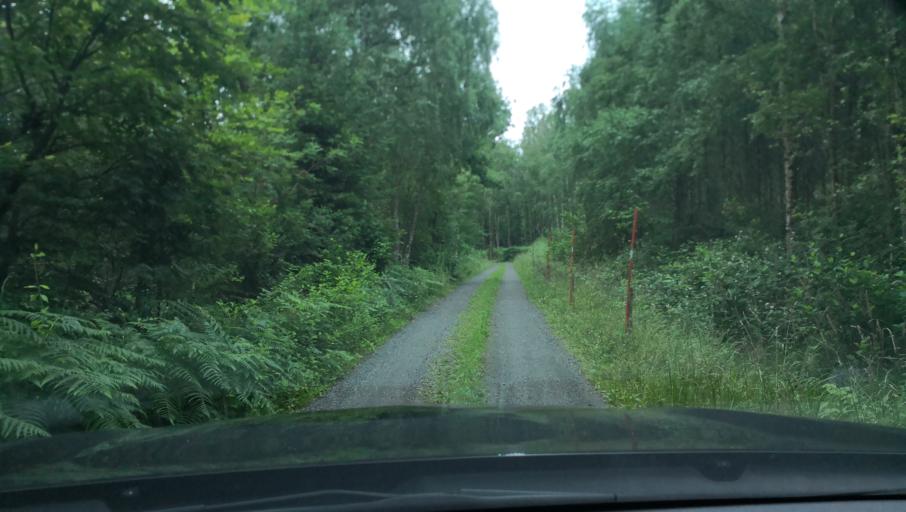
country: SE
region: Skane
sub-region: Kristianstads Kommun
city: Degeberga
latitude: 55.7089
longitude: 14.1182
